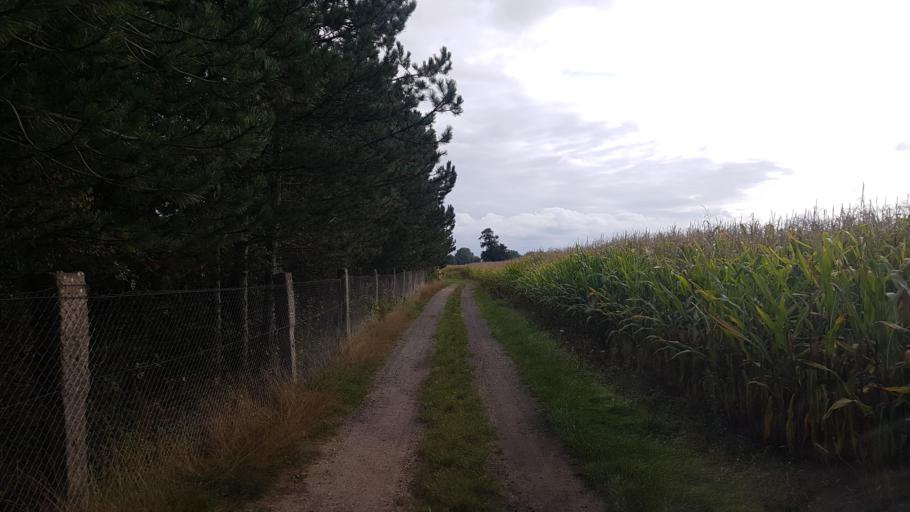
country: DE
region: Brandenburg
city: Elsterwerda
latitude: 51.4694
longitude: 13.4538
